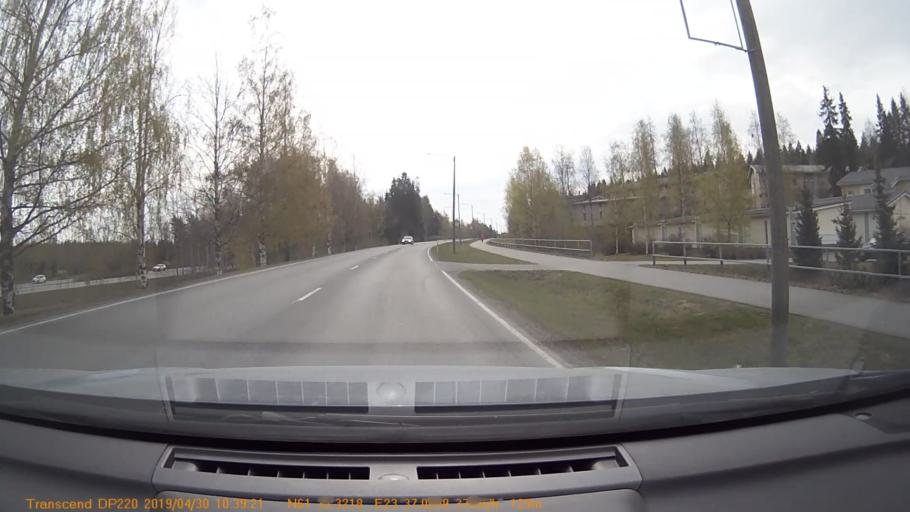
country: FI
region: Pirkanmaa
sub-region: Tampere
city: Yloejaervi
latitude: 61.5387
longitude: 23.6175
